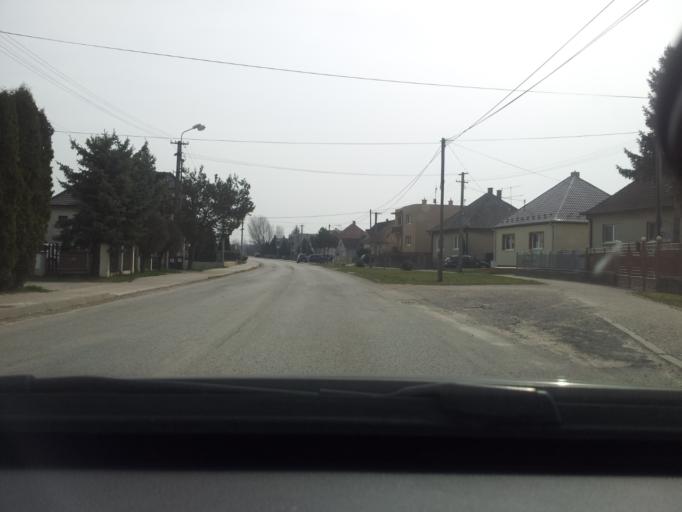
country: SK
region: Trnavsky
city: Leopoldov
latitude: 48.4581
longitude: 17.7190
